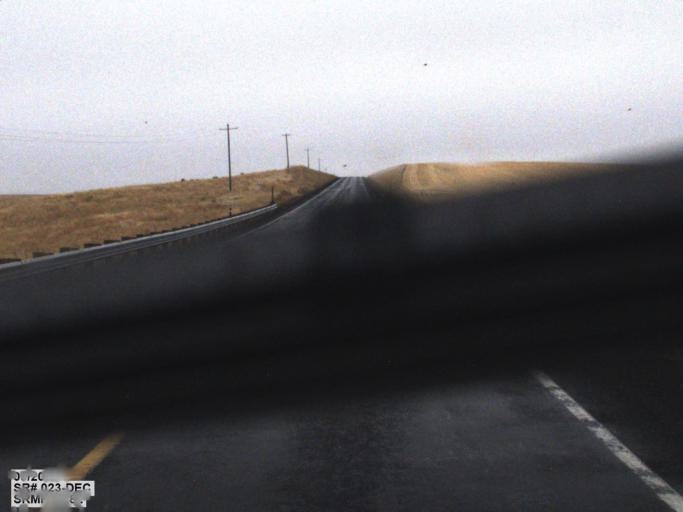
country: US
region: Washington
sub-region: Lincoln County
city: Davenport
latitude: 47.4783
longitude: -118.2396
